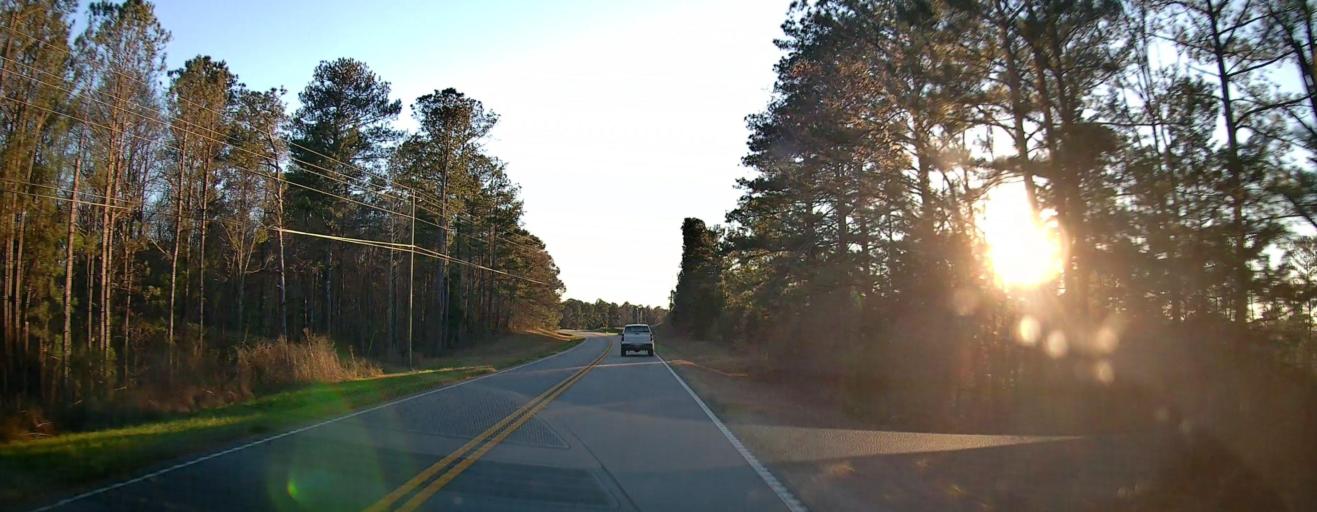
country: US
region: Alabama
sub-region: Lee County
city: Smiths Station
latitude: 32.6574
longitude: -84.9963
